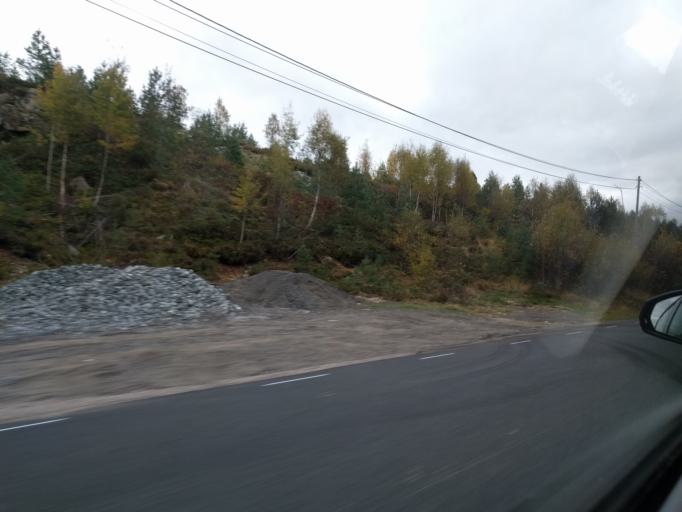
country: NO
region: Aust-Agder
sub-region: Iveland
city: Birketveit
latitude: 58.4385
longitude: 7.7875
